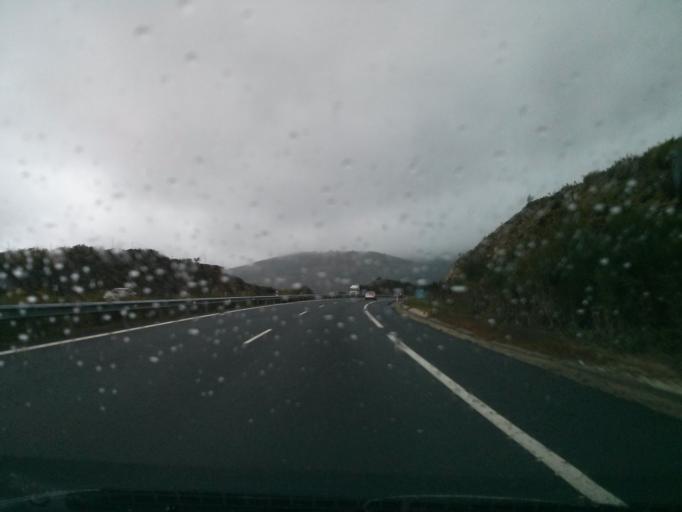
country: ES
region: Galicia
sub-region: Provincia de Pontevedra
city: Covelo
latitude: 42.1879
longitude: -8.3105
